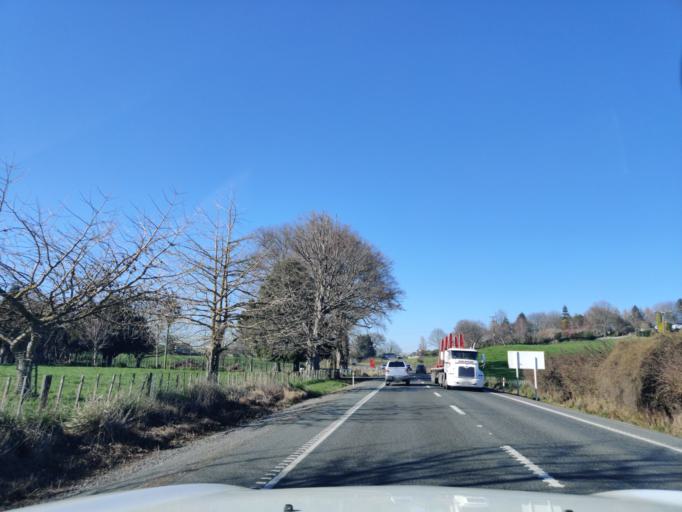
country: NZ
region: Waikato
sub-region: Matamata-Piako District
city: Matamata
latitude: -38.0094
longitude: 175.7725
